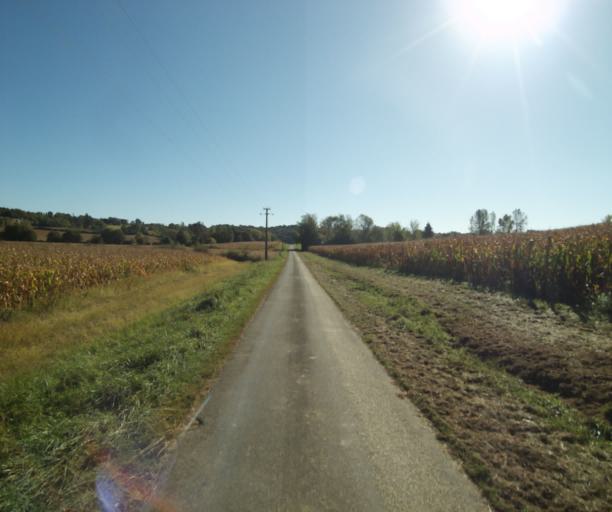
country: FR
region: Midi-Pyrenees
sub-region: Departement du Gers
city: Eauze
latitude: 43.8074
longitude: 0.1557
